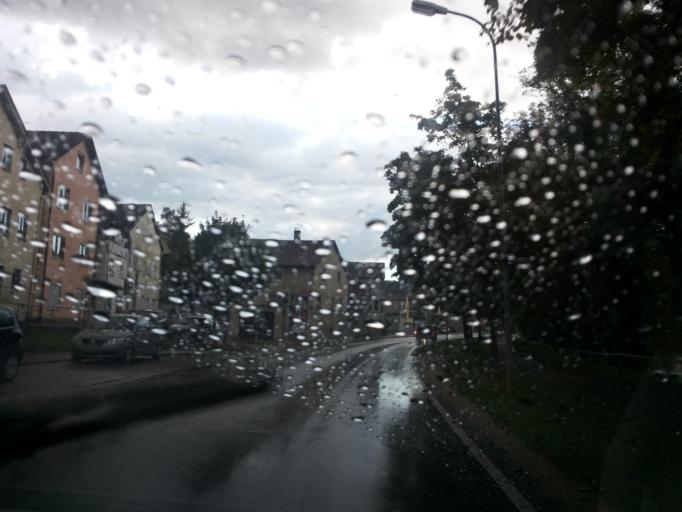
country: DE
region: Bavaria
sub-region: Upper Bavaria
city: Eichstaett
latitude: 48.8899
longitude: 11.1817
